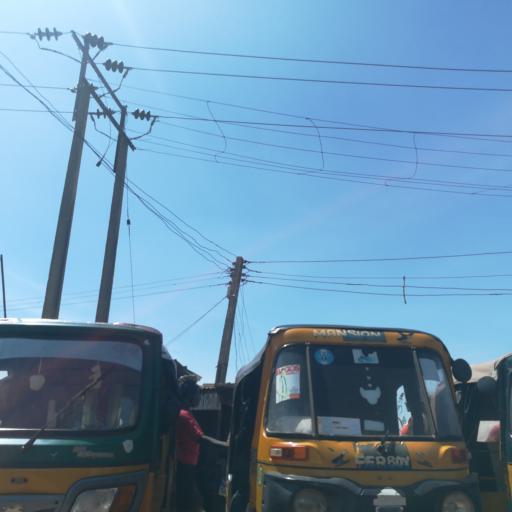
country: NG
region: Plateau
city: Bukuru
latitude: 9.7884
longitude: 8.8648
